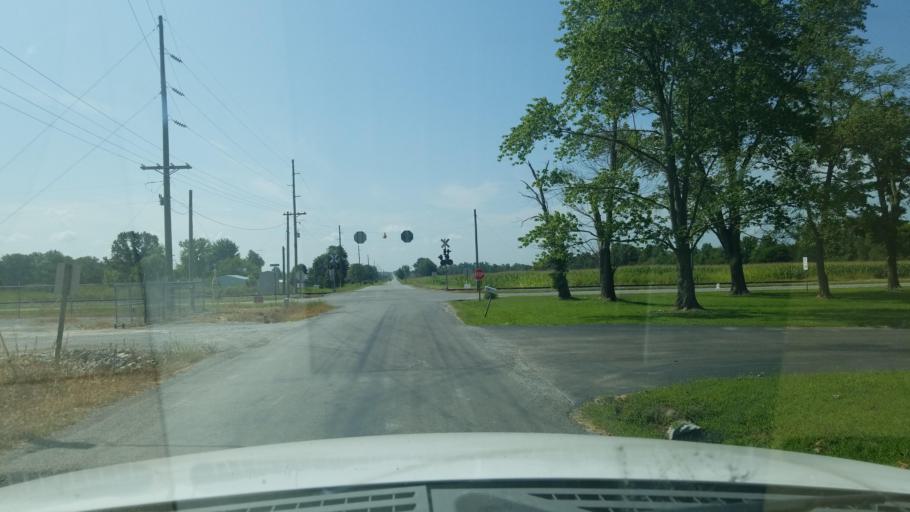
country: US
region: Illinois
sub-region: Saline County
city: Harrisburg
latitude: 37.8424
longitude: -88.6517
